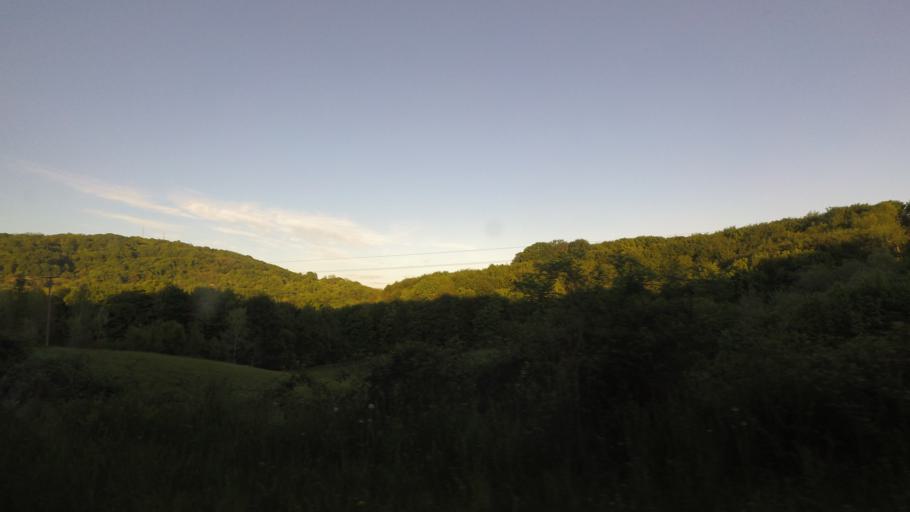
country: HR
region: Karlovacka
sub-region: Grad Karlovac
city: Karlovac
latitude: 45.4041
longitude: 15.5646
